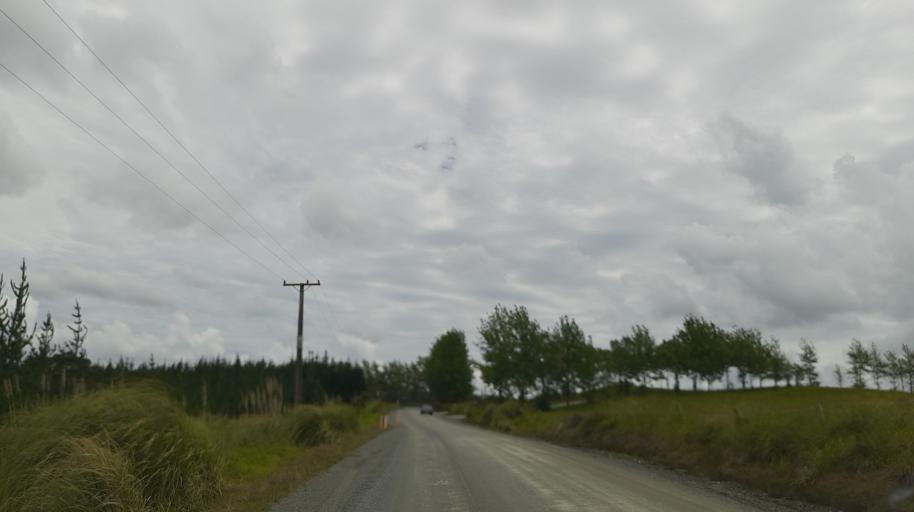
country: NZ
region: Auckland
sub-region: Auckland
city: Wellsford
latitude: -36.2339
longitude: 174.4397
